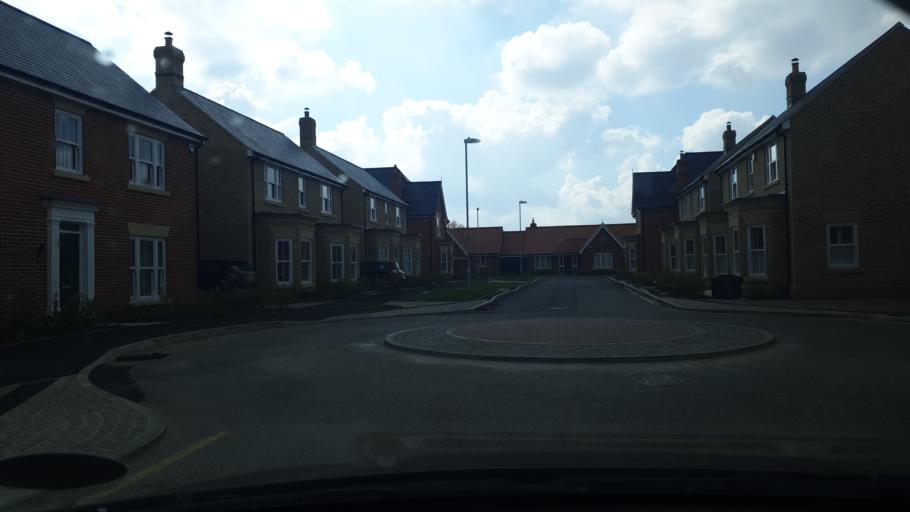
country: GB
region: England
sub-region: Essex
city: Manningtree
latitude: 51.9417
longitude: 1.0499
